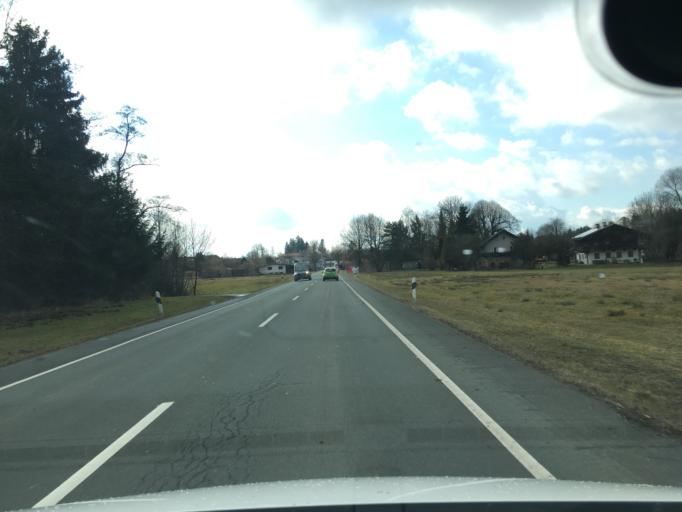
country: DE
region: Bavaria
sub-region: Upper Bavaria
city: Stephanskirchen
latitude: 47.8360
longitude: 12.1854
